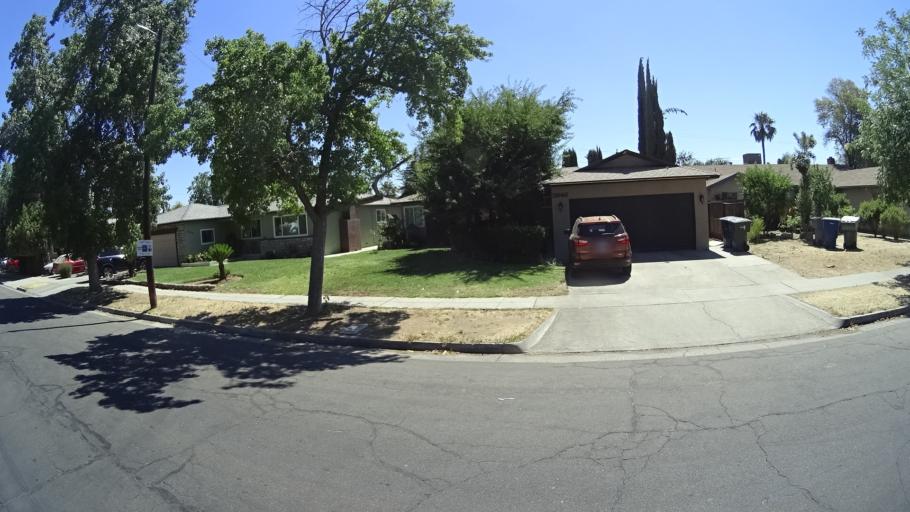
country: US
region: California
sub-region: Fresno County
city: Fresno
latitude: 36.7893
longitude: -119.8220
